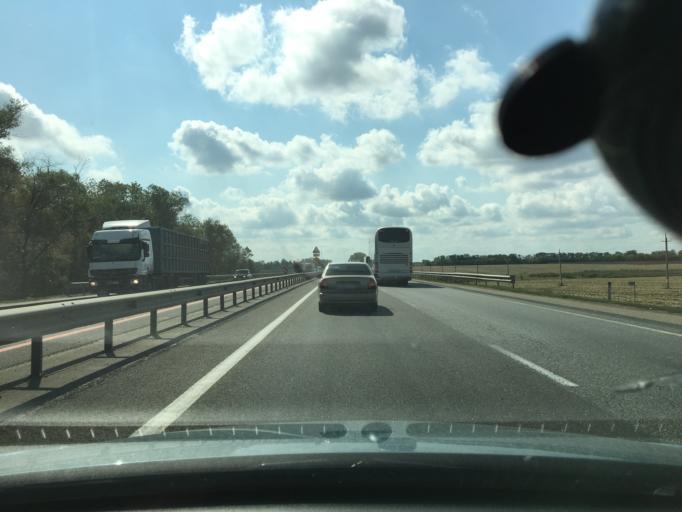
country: RU
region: Krasnodarskiy
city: Krasnoye
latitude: 46.6983
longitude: 39.6513
